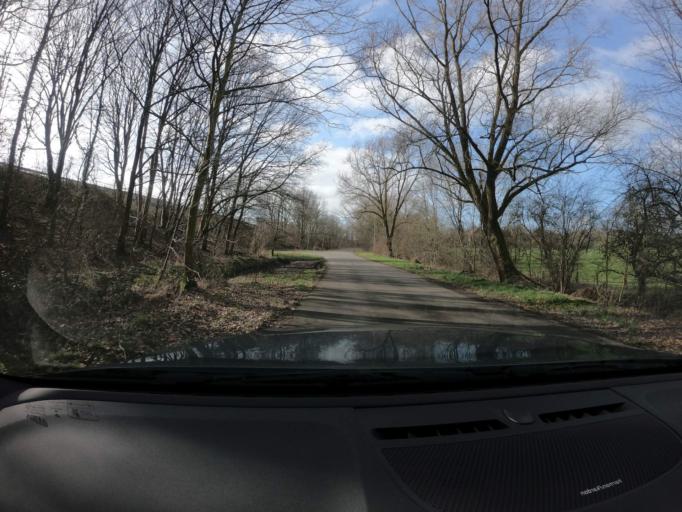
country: BE
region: Wallonia
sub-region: Province de Liege
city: Herve
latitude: 50.6368
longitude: 5.8292
